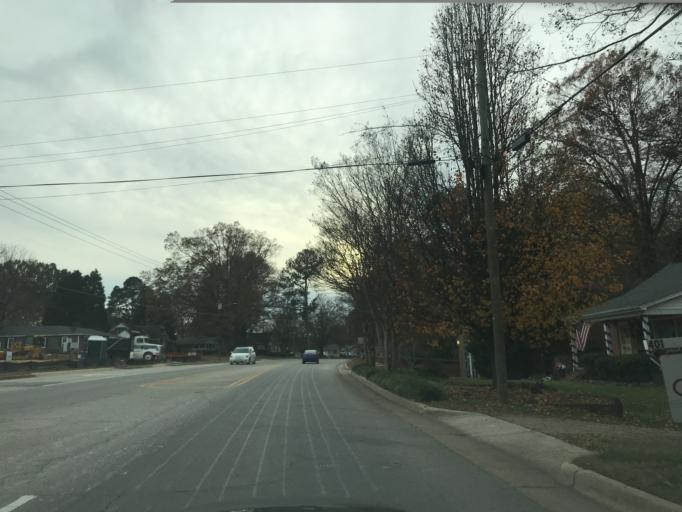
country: US
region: North Carolina
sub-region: Wake County
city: Cary
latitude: 35.7886
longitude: -78.7738
